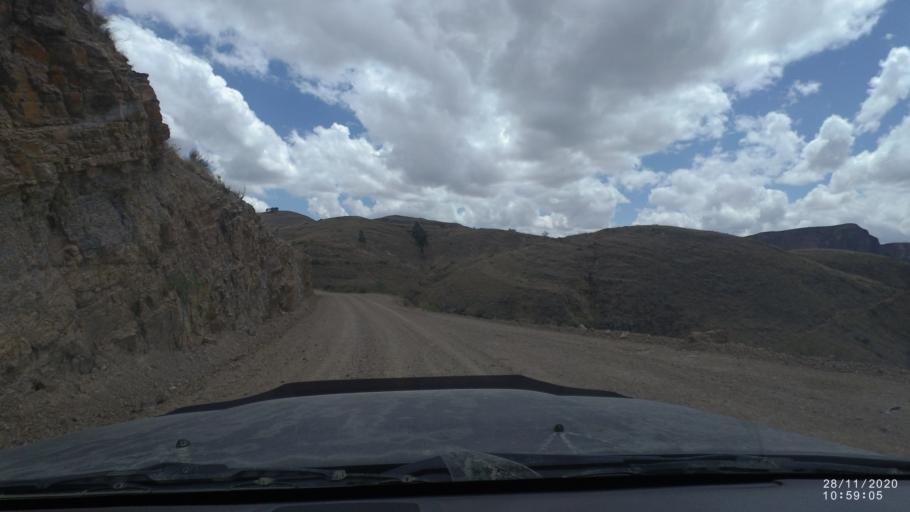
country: BO
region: Cochabamba
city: Capinota
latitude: -17.7750
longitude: -66.1082
